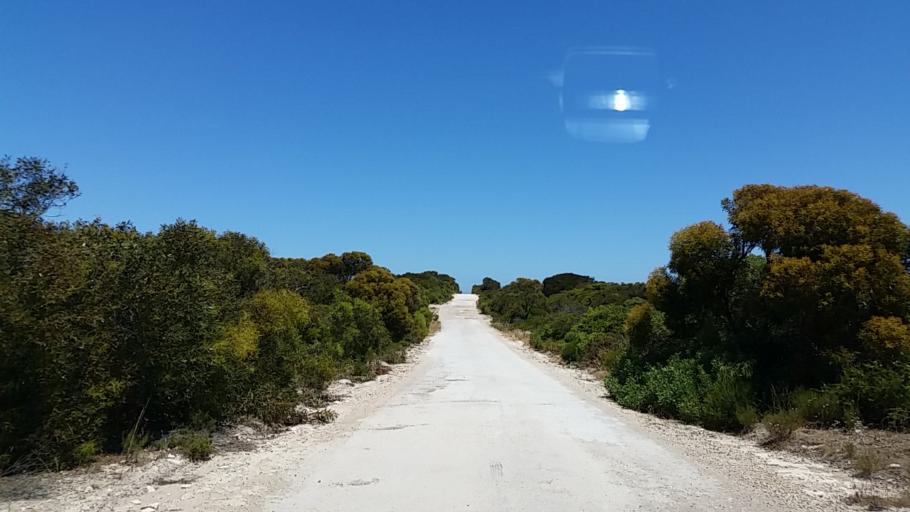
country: AU
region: South Australia
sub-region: Yorke Peninsula
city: Honiton
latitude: -35.2274
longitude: 137.1634
